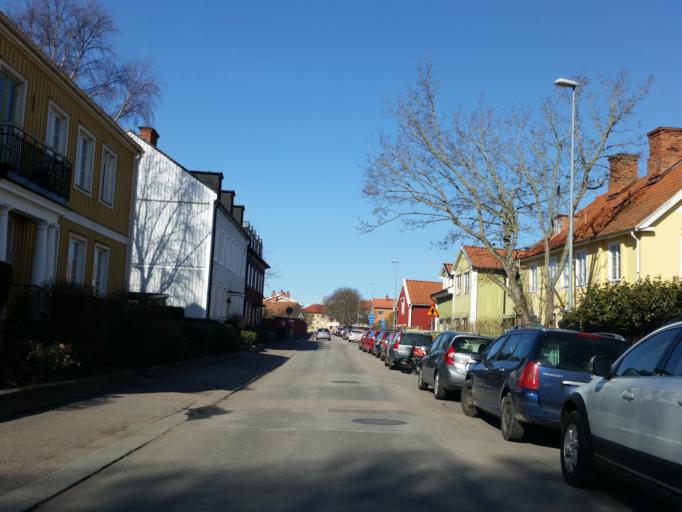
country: SE
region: Kalmar
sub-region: Kalmar Kommun
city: Kalmar
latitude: 56.6598
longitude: 16.3509
